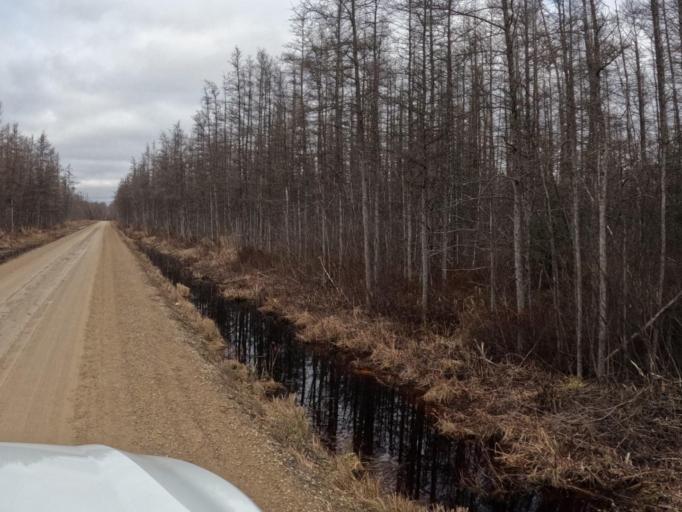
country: CA
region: Ontario
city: Shelburne
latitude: 43.9018
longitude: -80.4090
